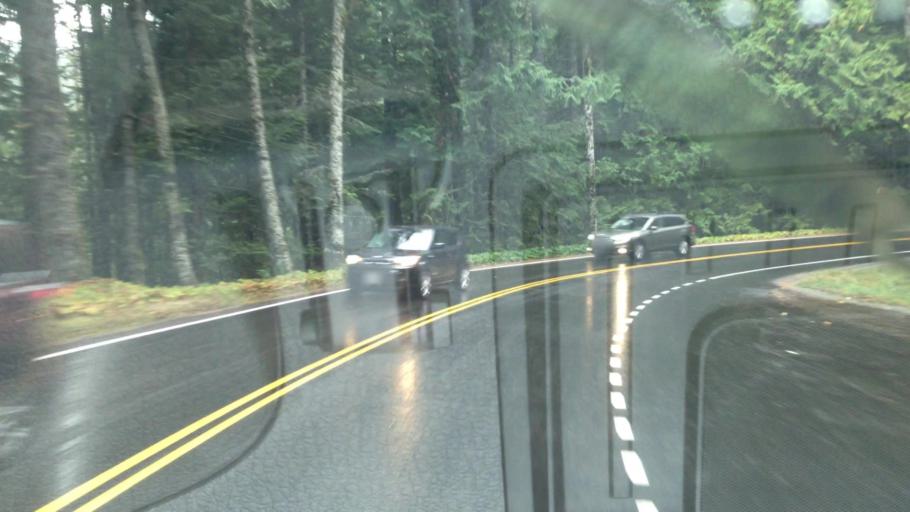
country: US
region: Washington
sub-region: Pierce County
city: Buckley
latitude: 46.7534
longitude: -121.8124
